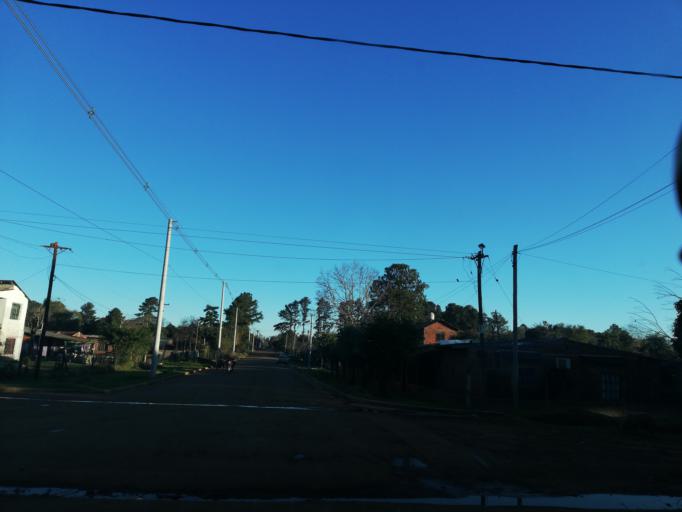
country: AR
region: Misiones
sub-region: Departamento de Candelaria
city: Candelaria
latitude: -27.4636
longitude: -55.7489
